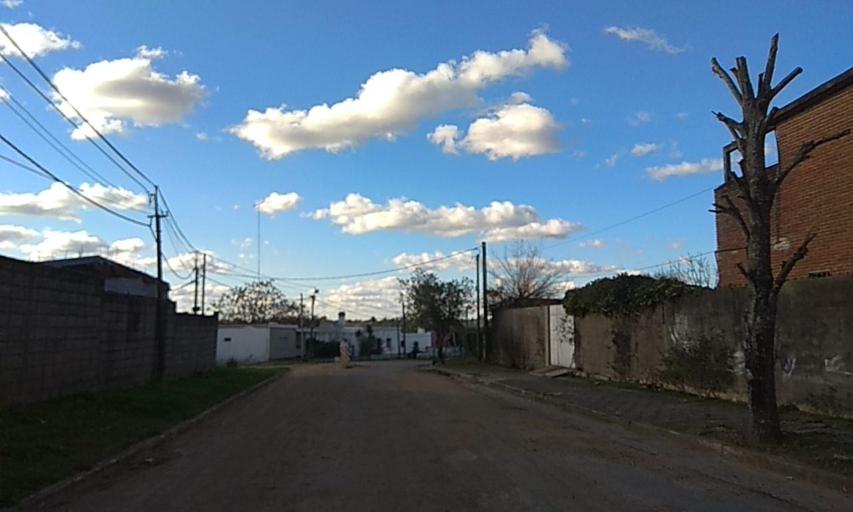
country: UY
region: Florida
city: Florida
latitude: -34.0983
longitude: -56.2289
